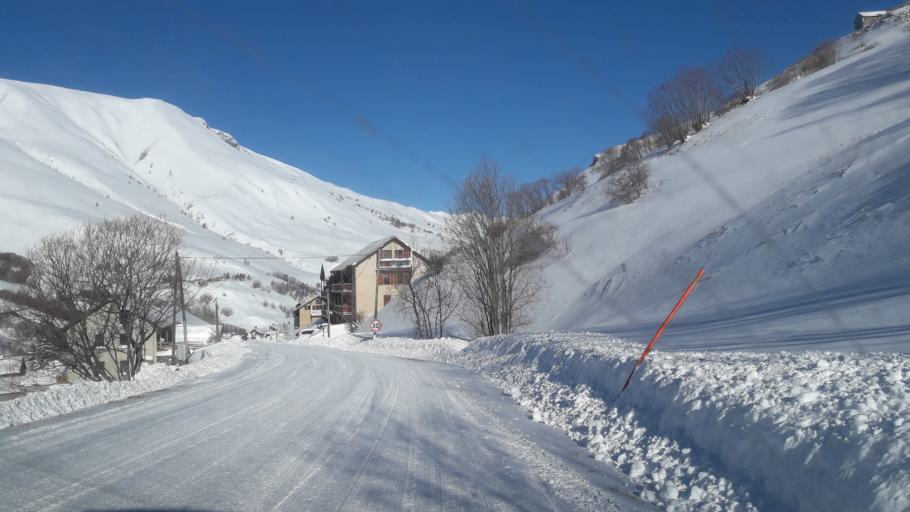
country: FR
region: Rhone-Alpes
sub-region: Departement de l'Isere
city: Mont-de-Lans
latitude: 45.0539
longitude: 6.2872
